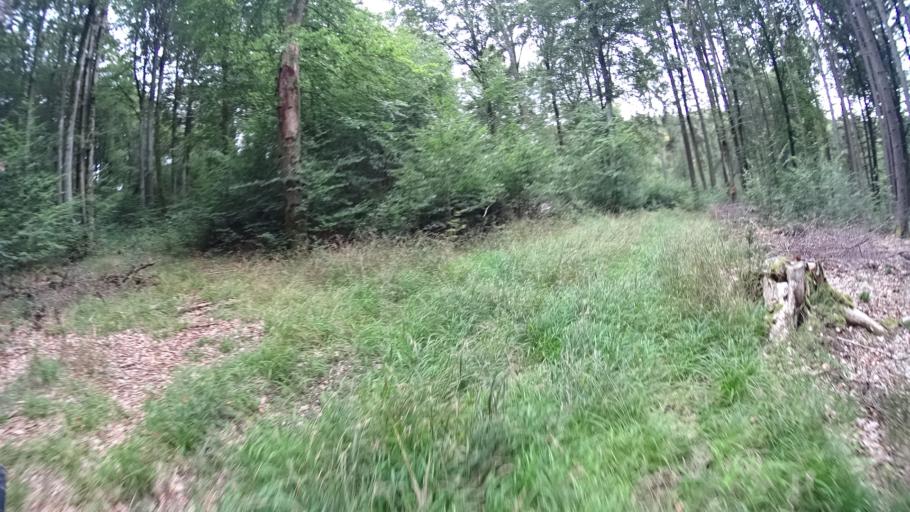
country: DE
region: Bavaria
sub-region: Upper Bavaria
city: Walting
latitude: 48.9134
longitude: 11.3105
